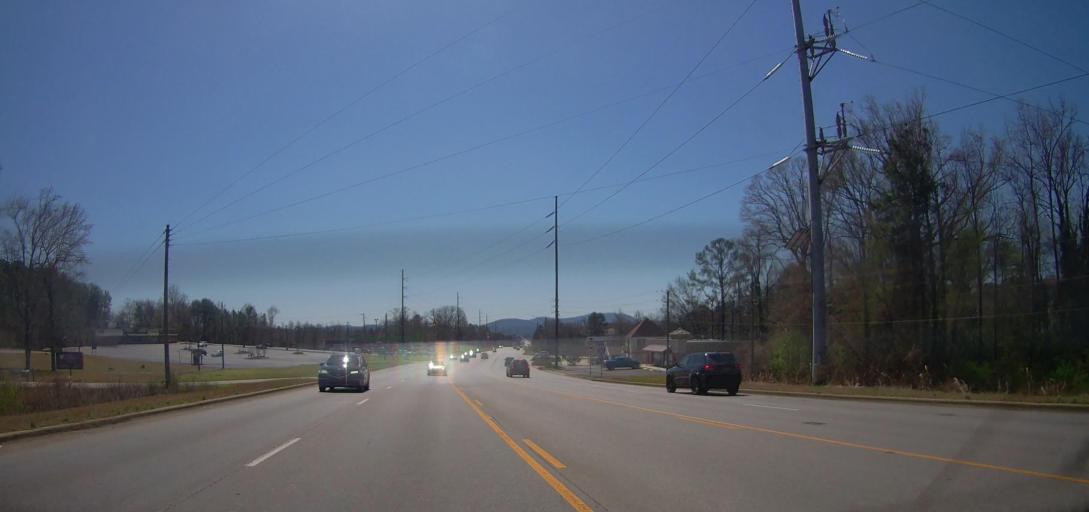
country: US
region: Alabama
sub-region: Calhoun County
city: Anniston
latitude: 33.6457
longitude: -85.7860
